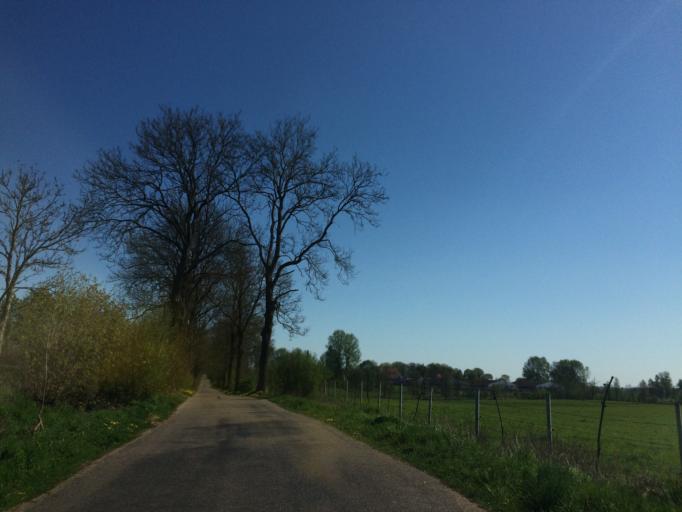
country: PL
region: Warmian-Masurian Voivodeship
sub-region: Powiat ostrodzki
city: Dabrowno
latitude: 53.4750
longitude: 19.9739
